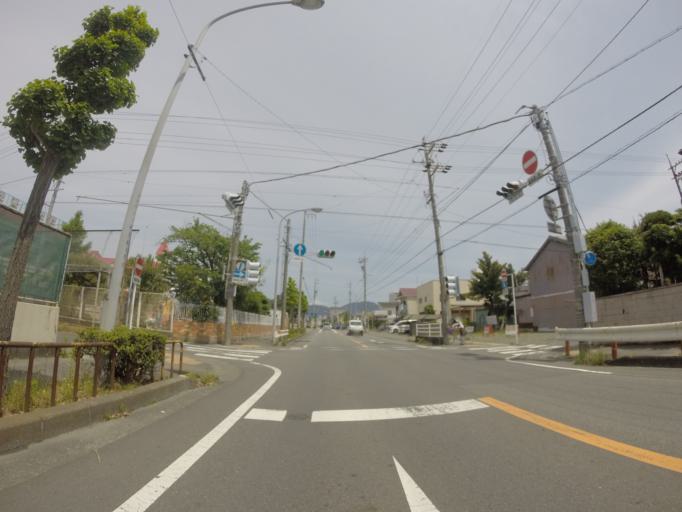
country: JP
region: Shizuoka
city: Yaizu
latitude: 34.8608
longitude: 138.3188
